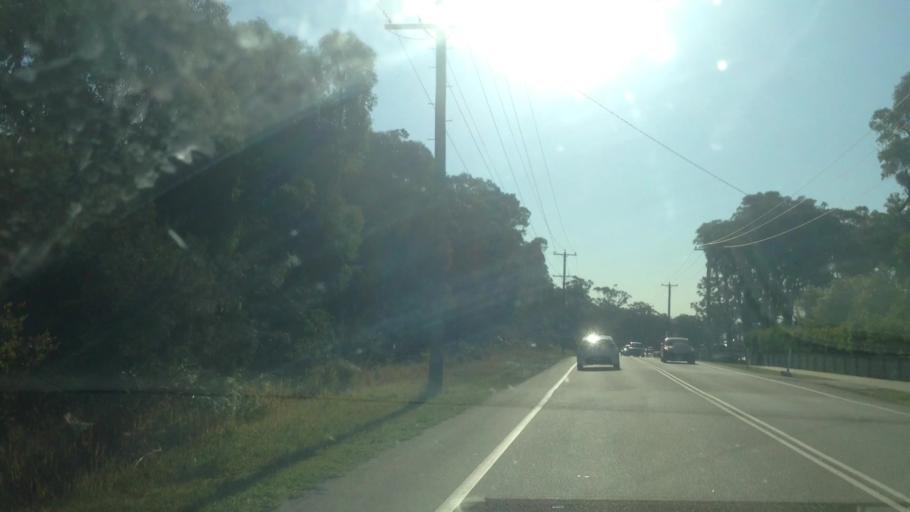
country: AU
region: New South Wales
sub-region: Lake Macquarie Shire
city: Dora Creek
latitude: -33.1129
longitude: 151.5125
